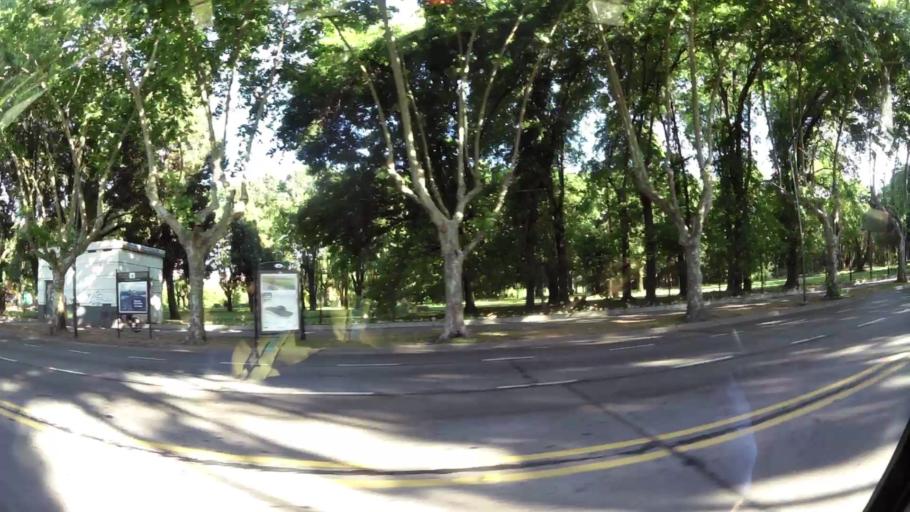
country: AR
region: Buenos Aires
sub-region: Partido de San Isidro
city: San Isidro
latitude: -34.4754
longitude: -58.5147
